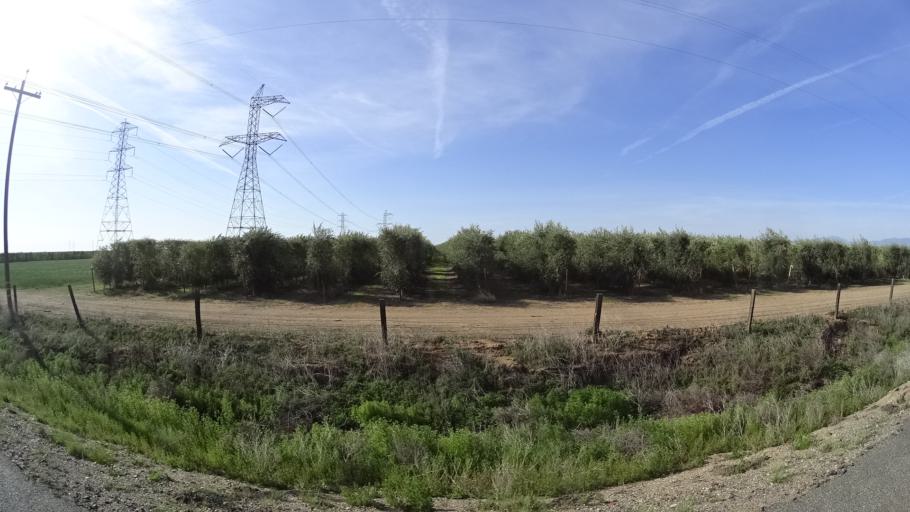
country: US
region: California
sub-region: Glenn County
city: Orland
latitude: 39.6685
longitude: -122.2746
